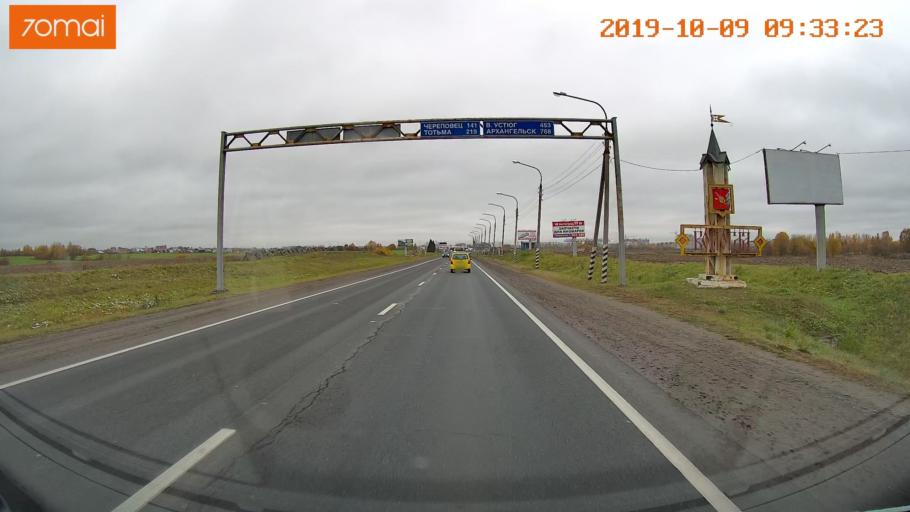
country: RU
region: Vologda
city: Vologda
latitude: 59.1676
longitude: 39.9150
